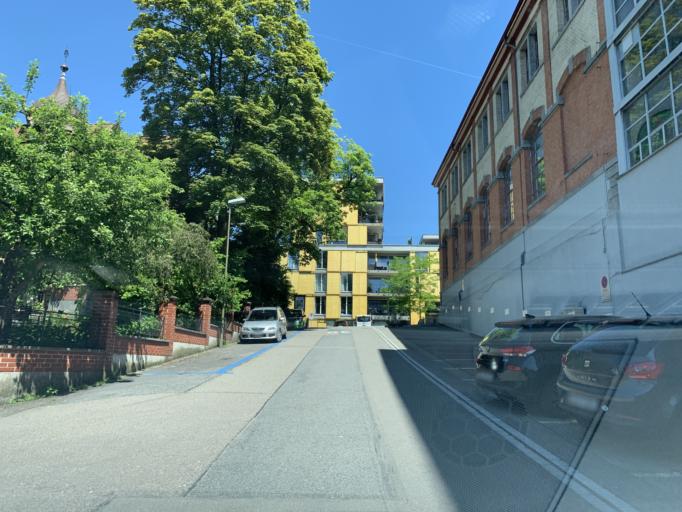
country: CH
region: Zurich
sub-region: Bezirk Winterthur
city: Stadt Winterthur (Kreis 1) / Lind
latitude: 47.5081
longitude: 8.7287
